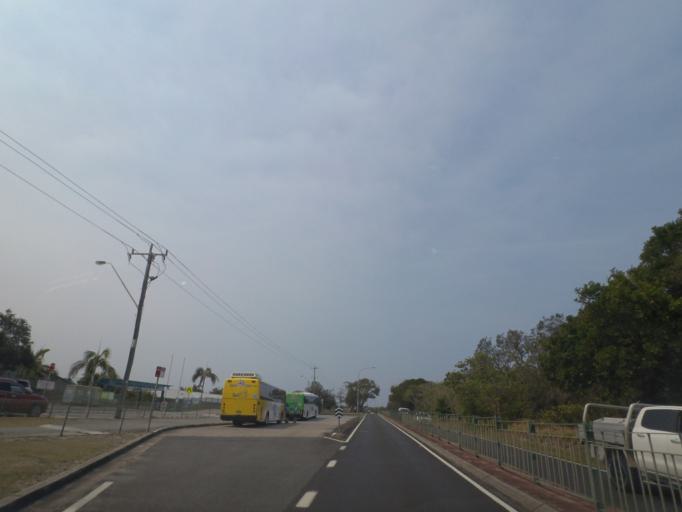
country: AU
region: New South Wales
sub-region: Tweed
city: Casuarina
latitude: -28.3389
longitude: 153.5729
